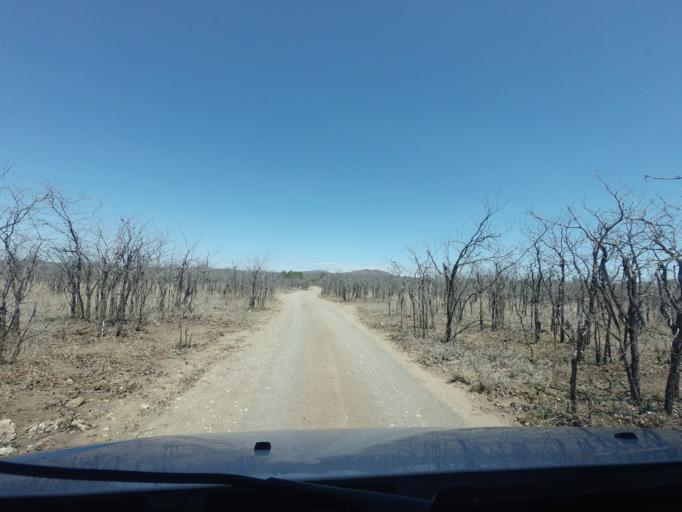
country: ZA
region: Limpopo
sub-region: Mopani District Municipality
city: Phalaborwa
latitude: -23.5837
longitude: 31.4495
